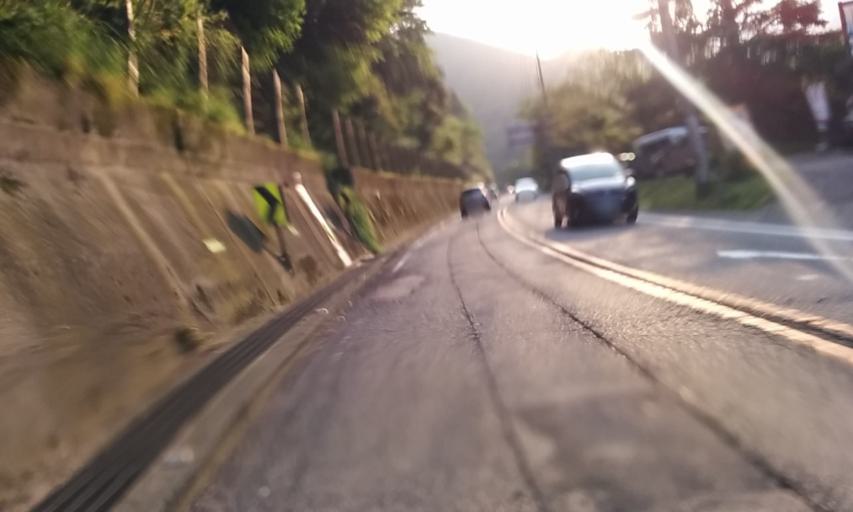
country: JP
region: Ehime
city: Saijo
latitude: 33.8440
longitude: 132.9991
